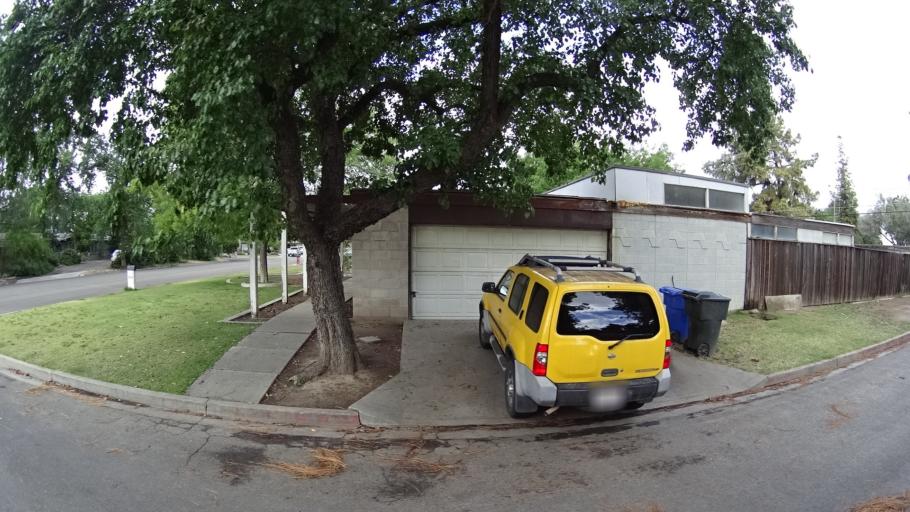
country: US
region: California
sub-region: Kings County
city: Hanford
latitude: 36.3497
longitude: -119.6573
